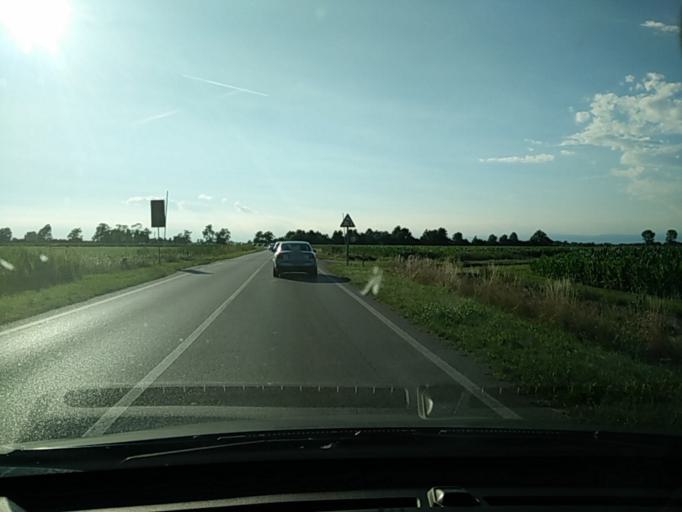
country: IT
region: Veneto
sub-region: Provincia di Venezia
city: Crepaldo
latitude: 45.5731
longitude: 12.7048
